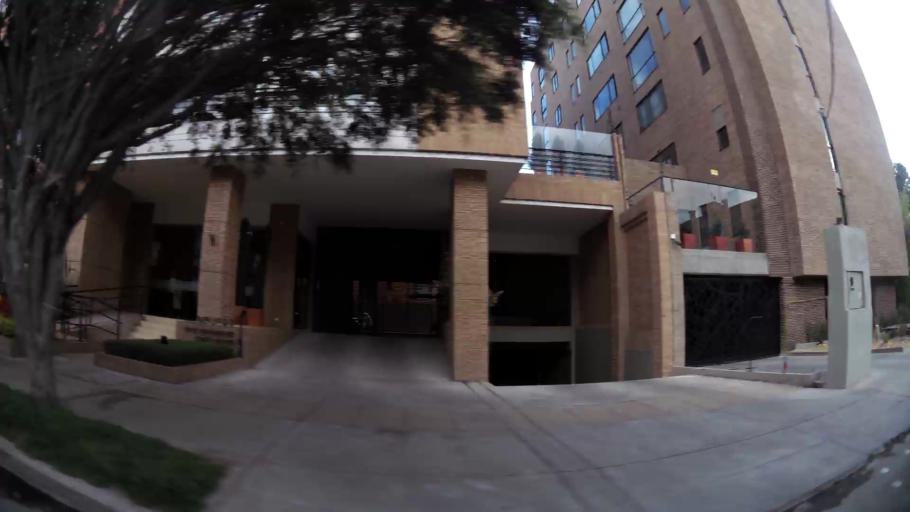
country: CO
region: Bogota D.C.
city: Barrio San Luis
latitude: 4.6890
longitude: -74.0507
